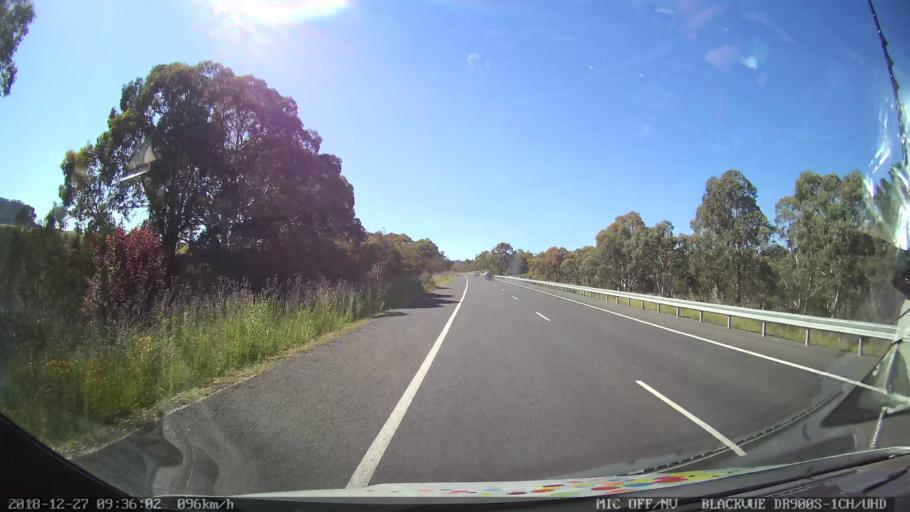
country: AU
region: New South Wales
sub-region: Lithgow
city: Portland
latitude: -33.2468
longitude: 150.0331
